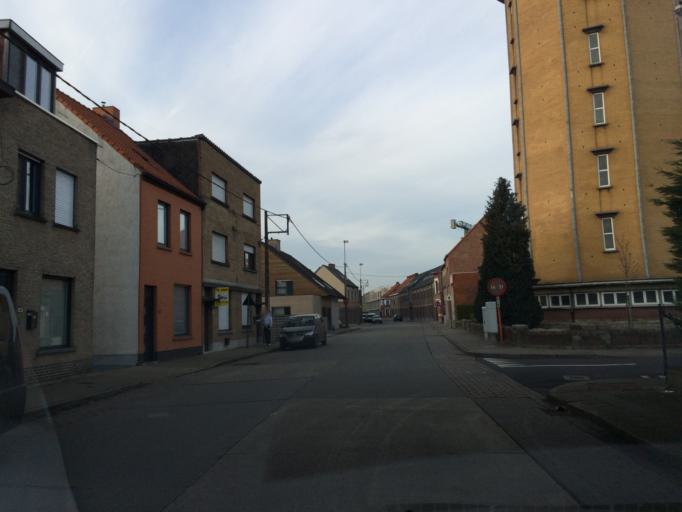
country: BE
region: Flanders
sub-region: Provincie West-Vlaanderen
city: Roeselare
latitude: 50.9368
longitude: 3.1301
